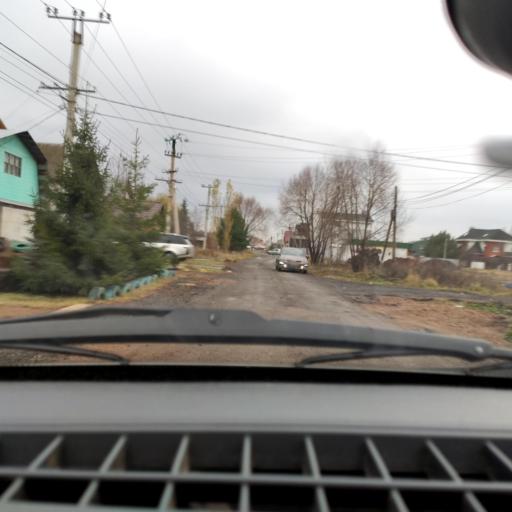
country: RU
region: Bashkortostan
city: Ufa
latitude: 54.6504
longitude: 55.9263
